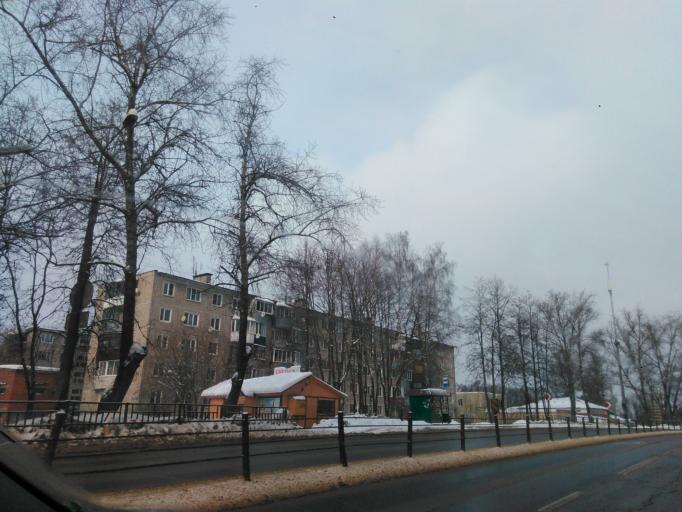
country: RU
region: Moskovskaya
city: Dedenevo
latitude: 56.2386
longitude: 37.5233
